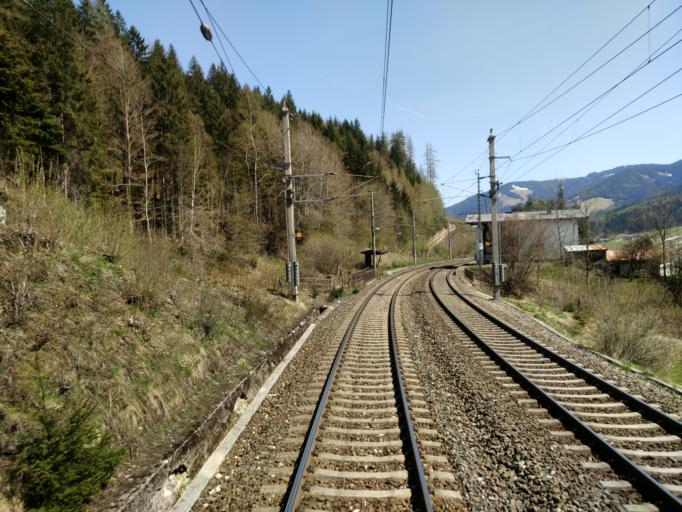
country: AT
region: Salzburg
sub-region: Politischer Bezirk Zell am See
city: Leogang
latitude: 47.4440
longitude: 12.7060
